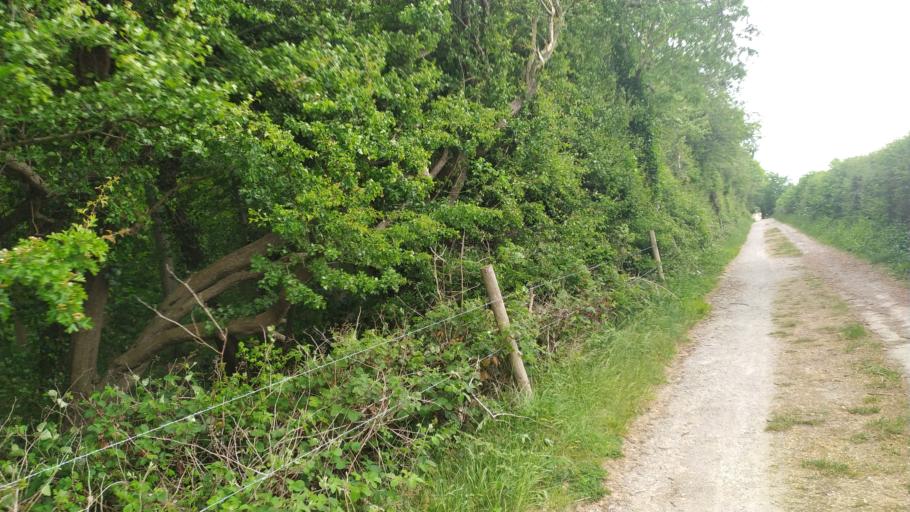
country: GB
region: England
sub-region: City and Borough of Leeds
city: Thorner
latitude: 53.8588
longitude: -1.3912
